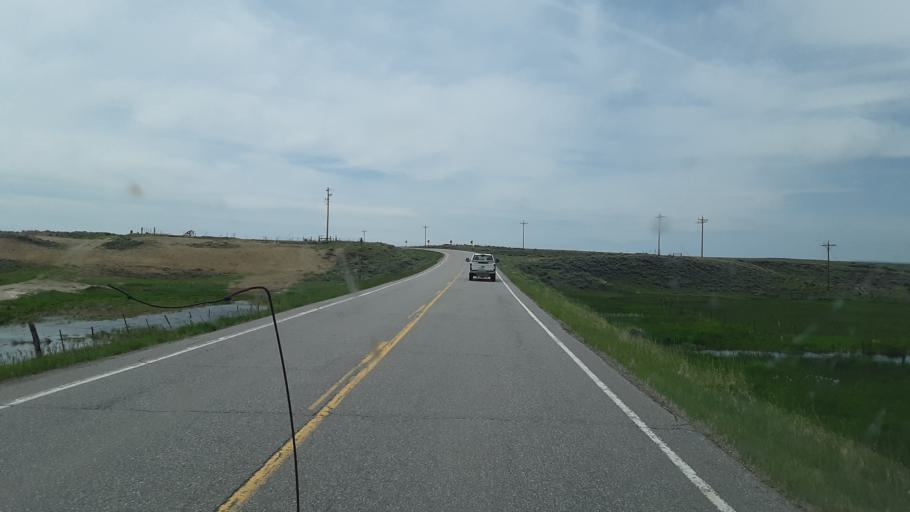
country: US
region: Colorado
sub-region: Jackson County
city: Walden
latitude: 40.6321
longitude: -106.3971
